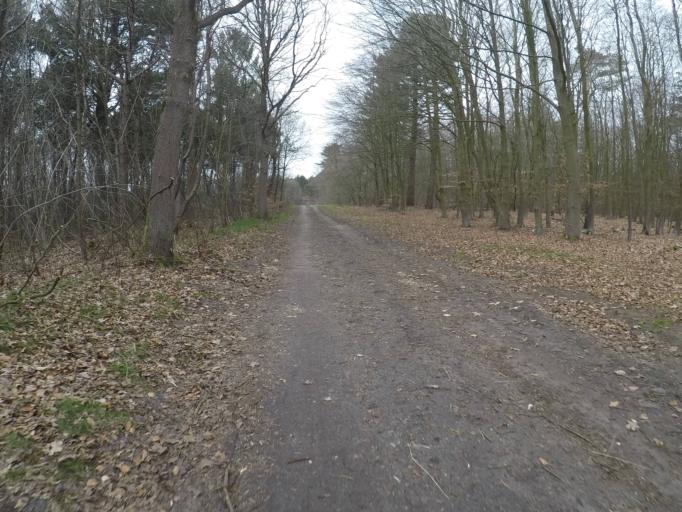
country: DE
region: Lower Saxony
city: Nordholz
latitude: 53.7987
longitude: 8.6248
